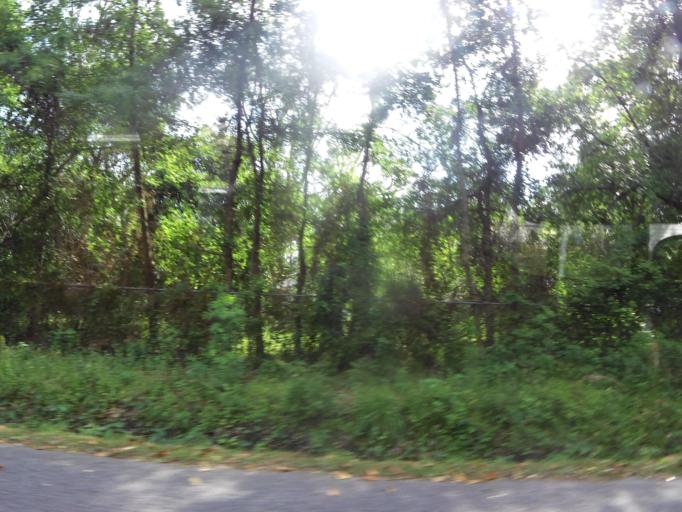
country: US
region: Florida
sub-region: Duval County
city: Jacksonville
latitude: 30.3165
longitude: -81.7242
